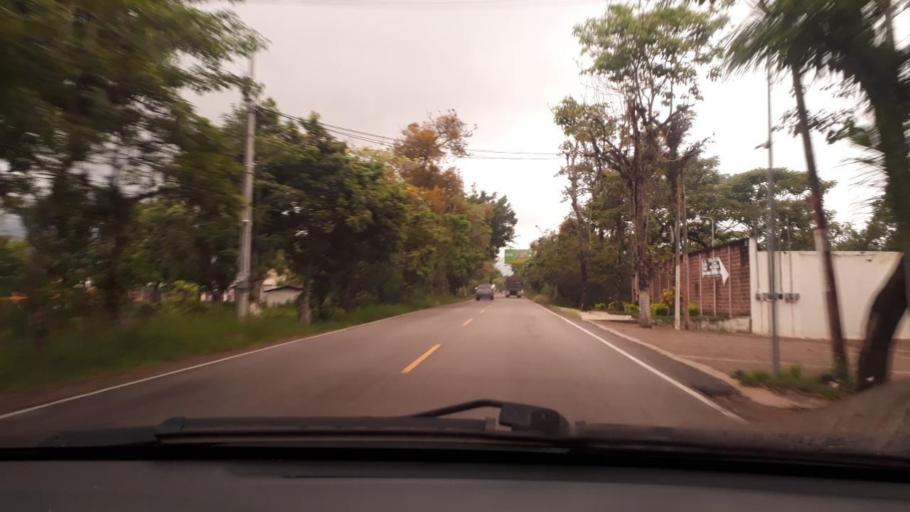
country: GT
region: Chiquimula
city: Esquipulas
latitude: 14.5651
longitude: -89.3188
